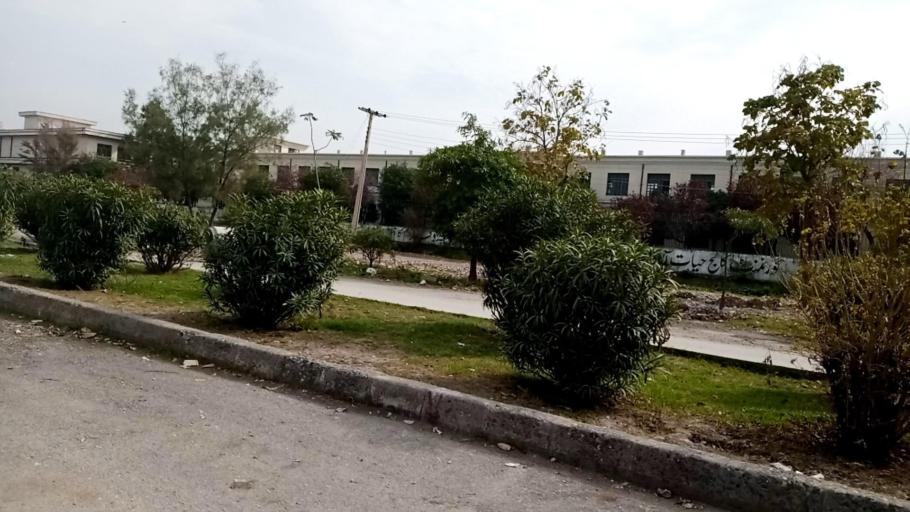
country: PK
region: Khyber Pakhtunkhwa
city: Peshawar
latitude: 33.9564
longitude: 71.4435
